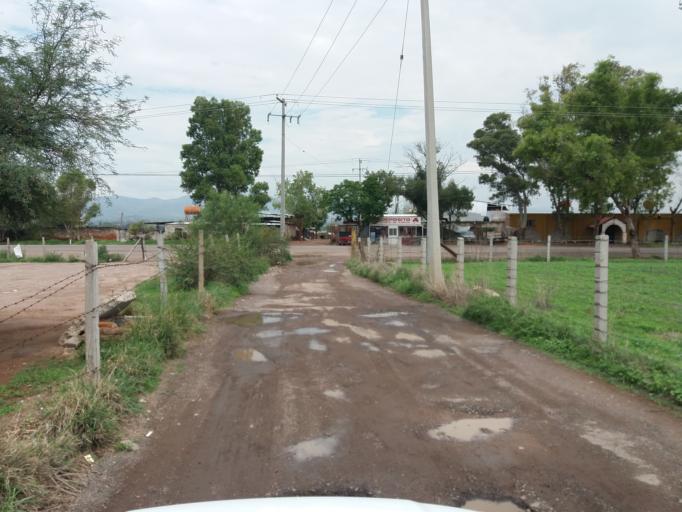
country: MX
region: Aguascalientes
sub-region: Aguascalientes
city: La Loma de los Negritos
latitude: 21.8325
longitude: -102.3288
